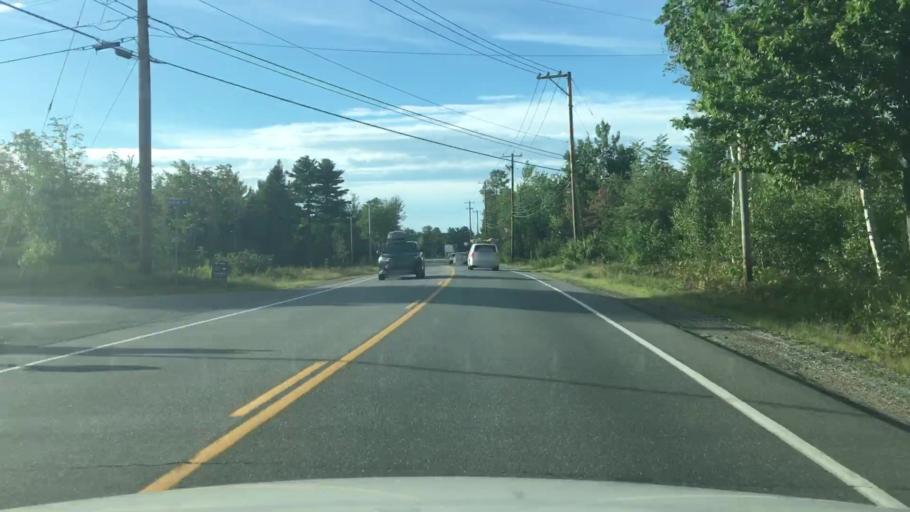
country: US
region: Maine
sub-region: Hancock County
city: Ellsworth
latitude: 44.5006
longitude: -68.3823
